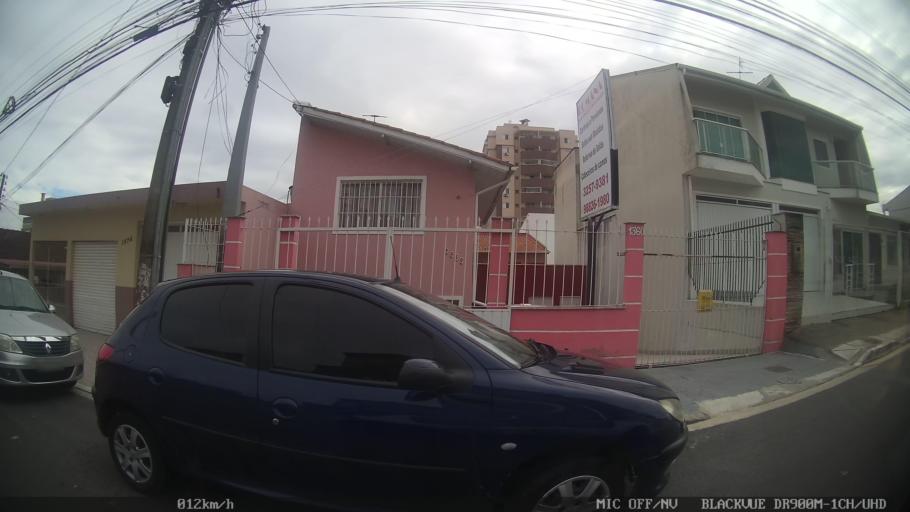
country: BR
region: Santa Catarina
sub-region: Sao Jose
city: Campinas
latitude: -27.5827
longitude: -48.6092
